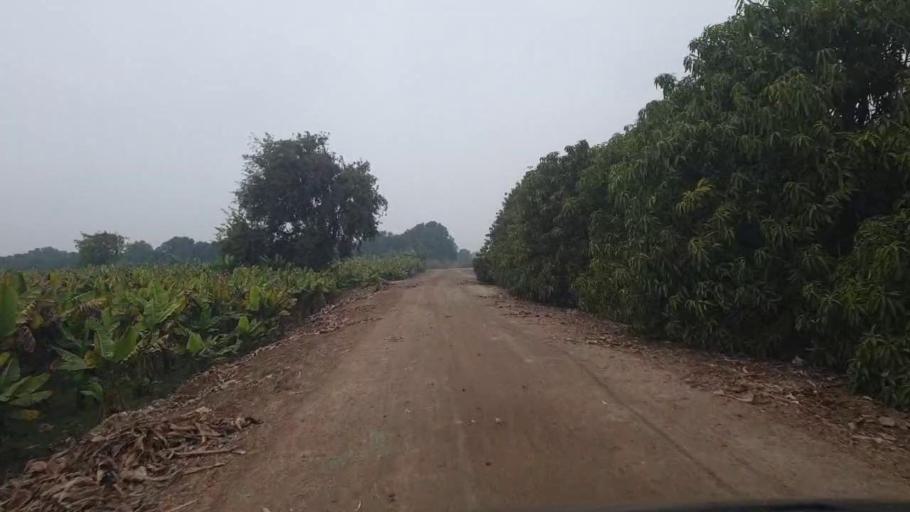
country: PK
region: Sindh
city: Tando Adam
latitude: 25.8028
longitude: 68.6649
